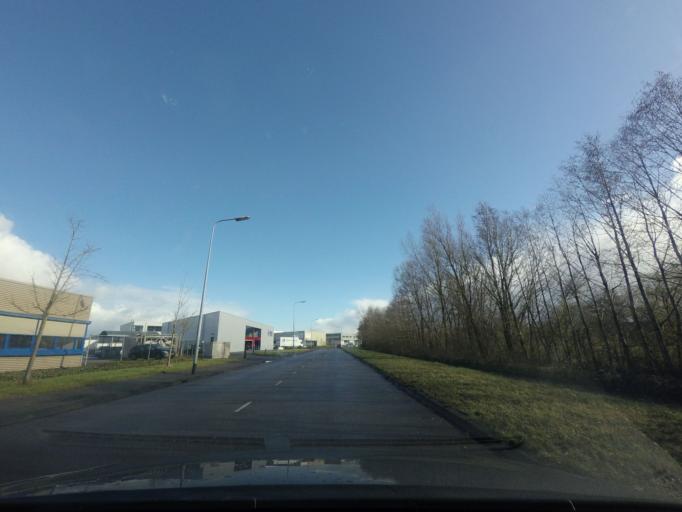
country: NL
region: Groningen
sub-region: Gemeente Groningen
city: Oosterpark
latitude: 53.2125
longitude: 6.6083
